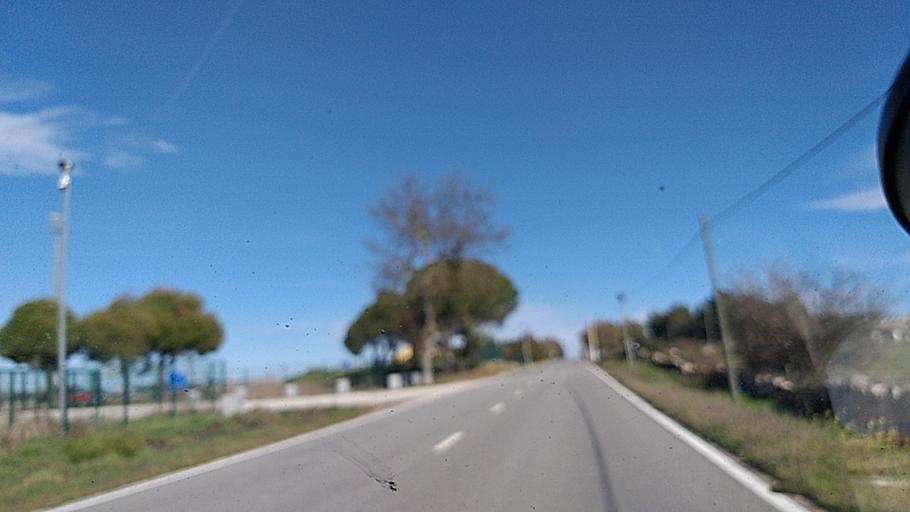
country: ES
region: Castille and Leon
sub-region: Provincia de Salamanca
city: Fuentes de Onoro
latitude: 40.6161
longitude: -6.8609
